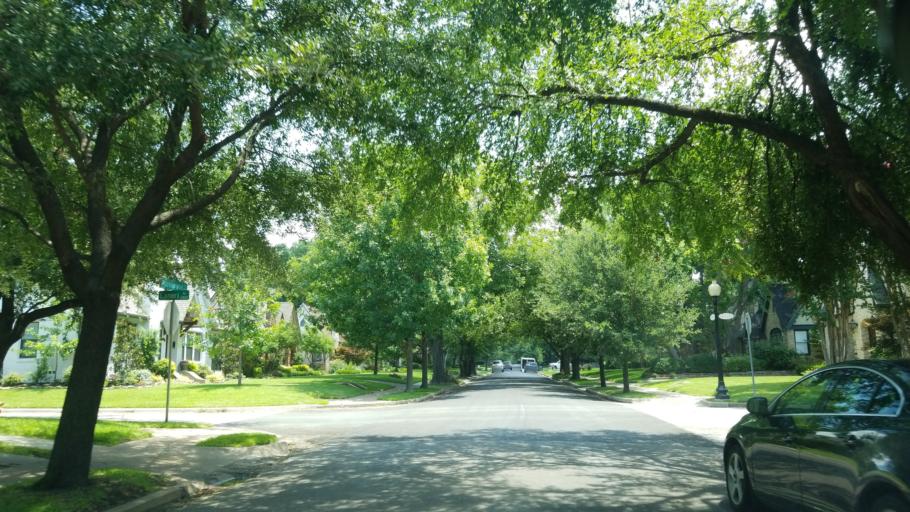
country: US
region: Texas
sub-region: Dallas County
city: Highland Park
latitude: 32.8290
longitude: -96.7802
